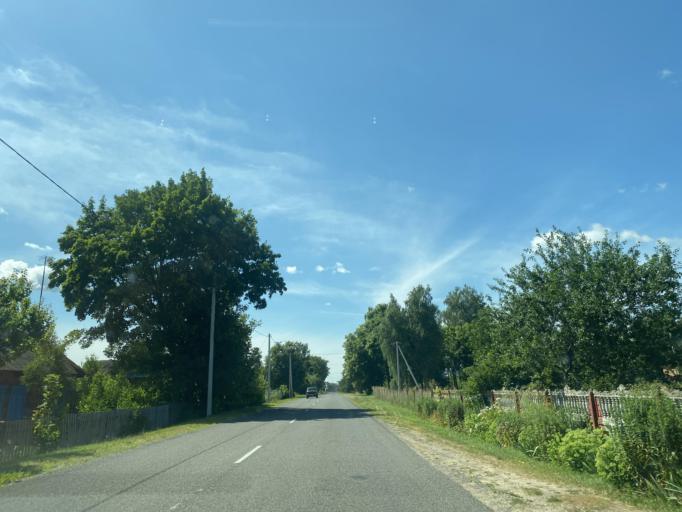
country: BY
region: Brest
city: Ivanava
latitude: 52.2014
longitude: 25.6146
